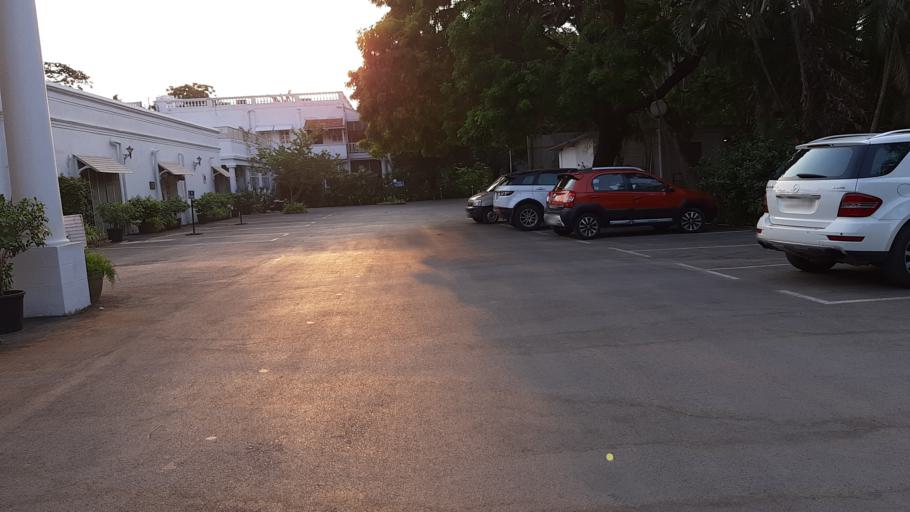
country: IN
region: Tamil Nadu
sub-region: Chennai
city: Gandhi Nagar
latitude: 13.0252
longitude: 80.2471
